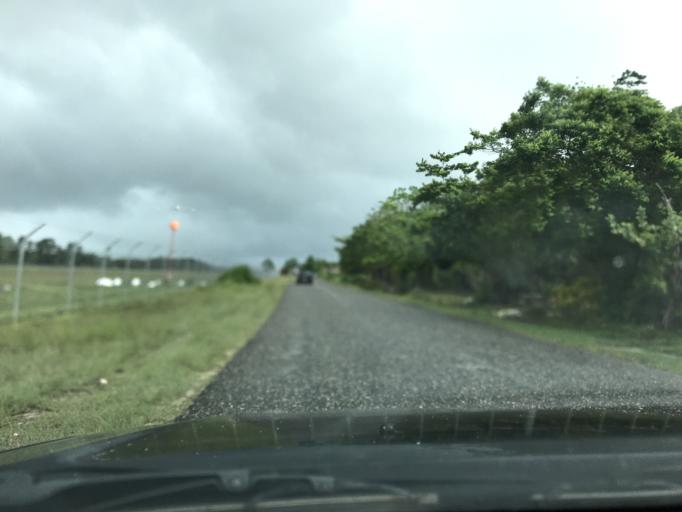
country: SB
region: Western Province
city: Gizo
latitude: -8.3249
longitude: 157.2689
